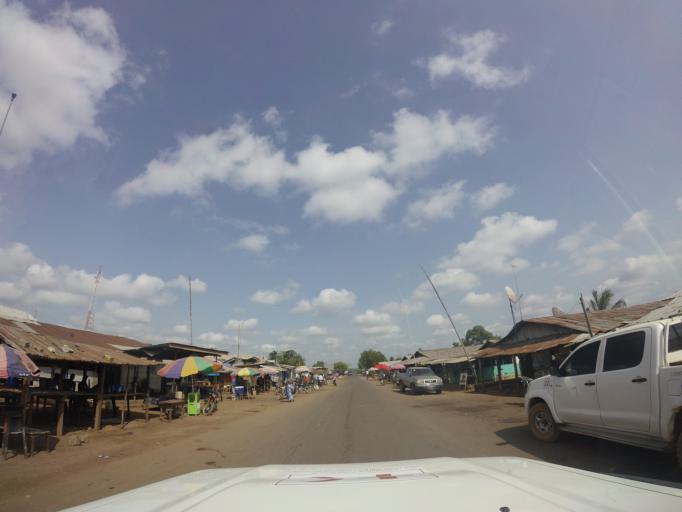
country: LR
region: Bomi
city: Tubmanburg
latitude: 6.7148
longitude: -10.9721
